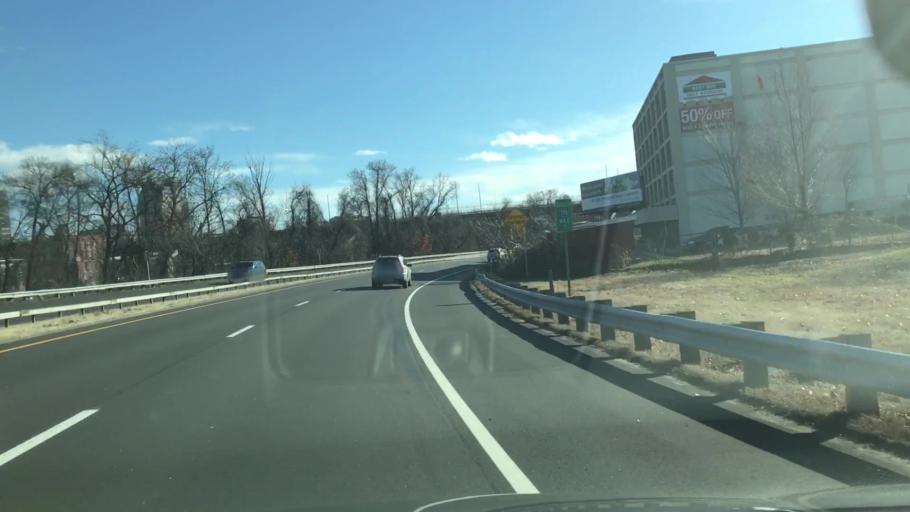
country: US
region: New Hampshire
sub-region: Hillsborough County
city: Manchester
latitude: 42.9966
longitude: -71.4713
